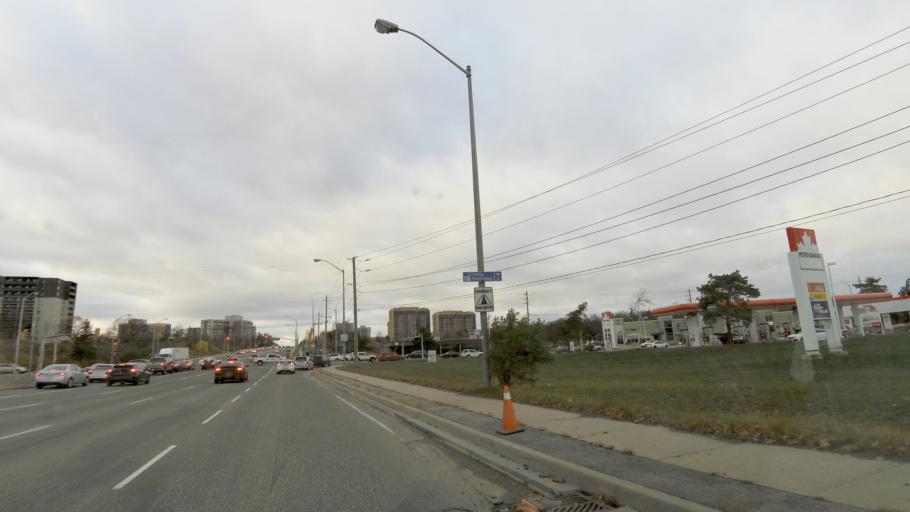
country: CA
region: Ontario
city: Oakville
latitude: 43.4639
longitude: -79.6861
